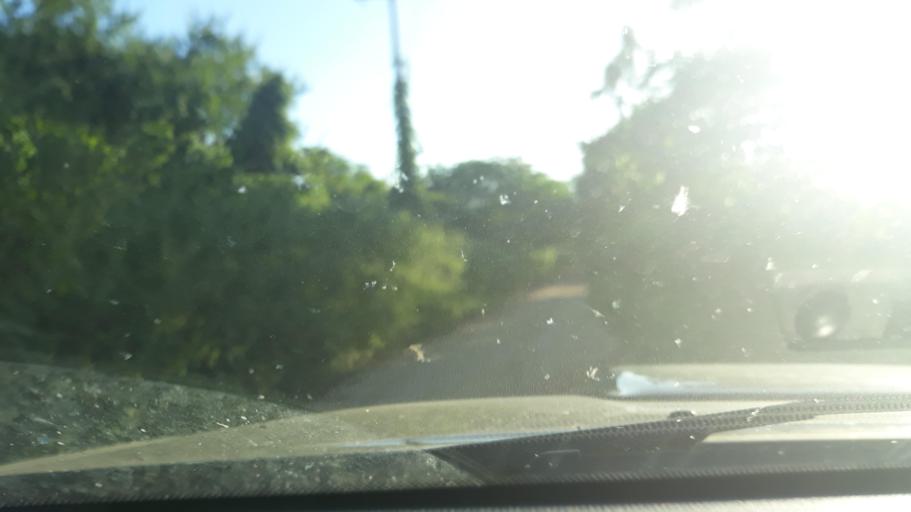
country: BR
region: Bahia
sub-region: Riacho De Santana
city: Riacho de Santana
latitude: -13.8425
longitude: -42.7380
